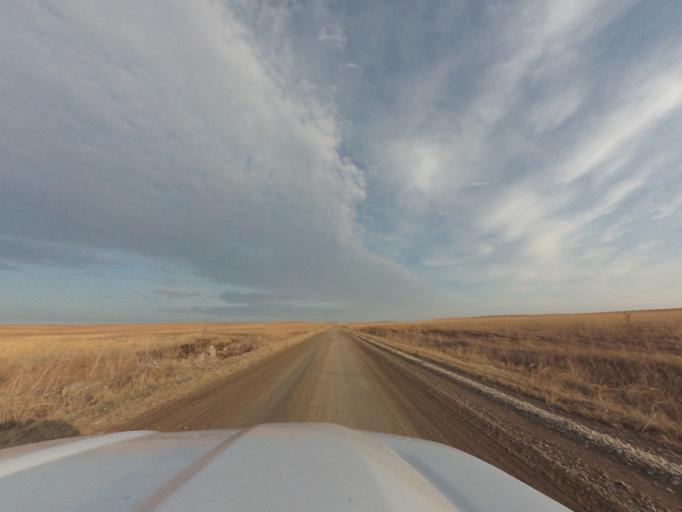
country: US
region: Kansas
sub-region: Morris County
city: Council Grove
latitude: 38.4999
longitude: -96.4102
